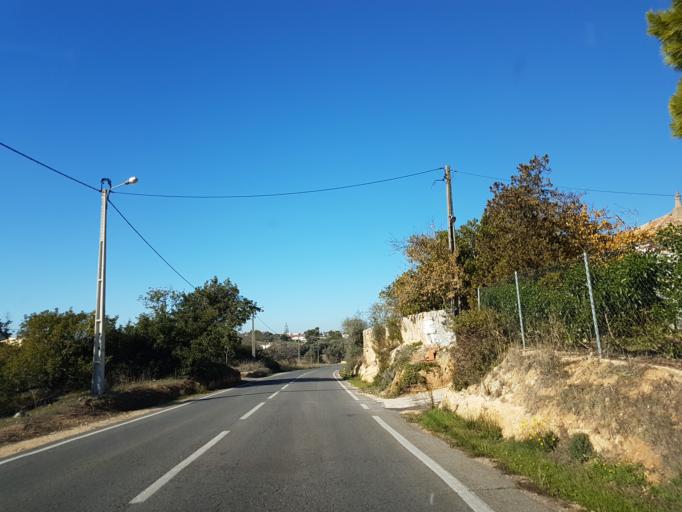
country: PT
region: Faro
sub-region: Lagoa
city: Carvoeiro
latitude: 37.1120
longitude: -8.4496
